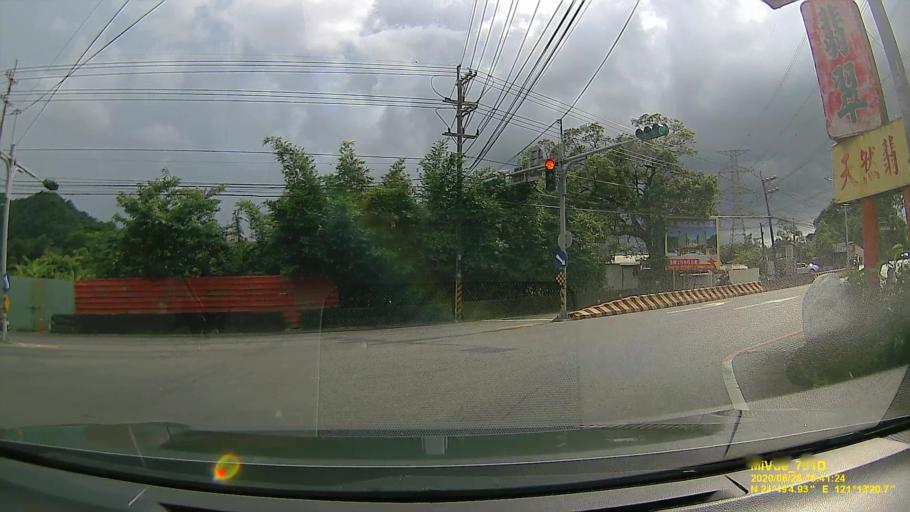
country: TW
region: Taiwan
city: Daxi
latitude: 24.8180
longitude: 121.2224
